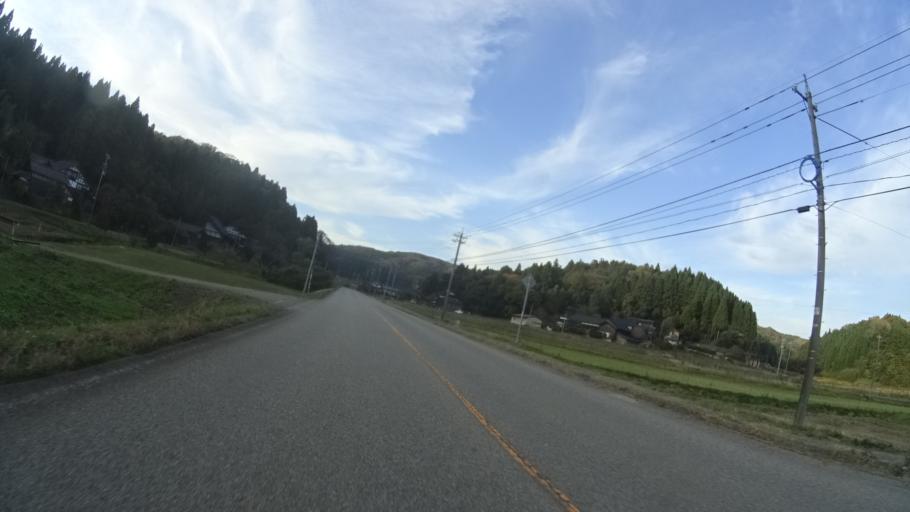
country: JP
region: Ishikawa
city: Nanao
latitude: 37.1921
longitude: 136.7170
